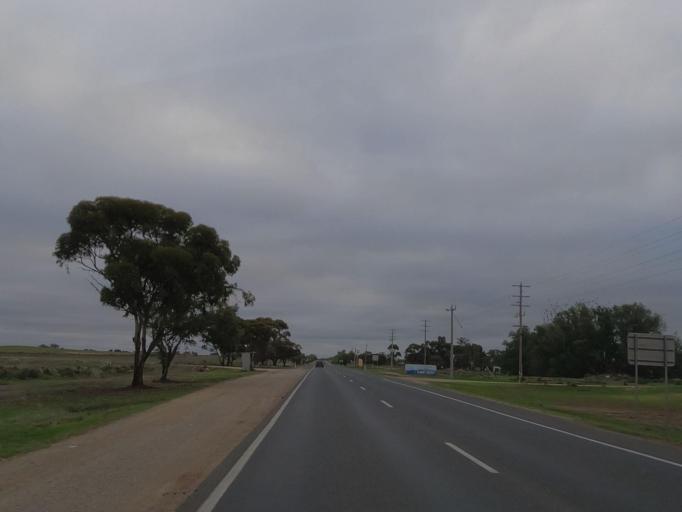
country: AU
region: Victoria
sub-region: Swan Hill
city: Swan Hill
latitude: -35.4519
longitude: 143.6254
